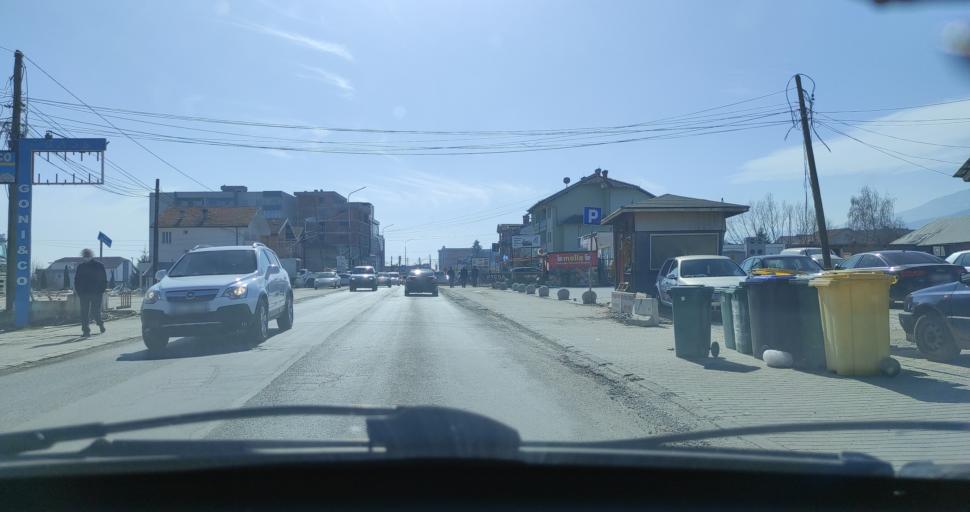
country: XK
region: Gjakova
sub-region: Komuna e Decanit
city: Decan
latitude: 42.5461
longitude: 20.2904
